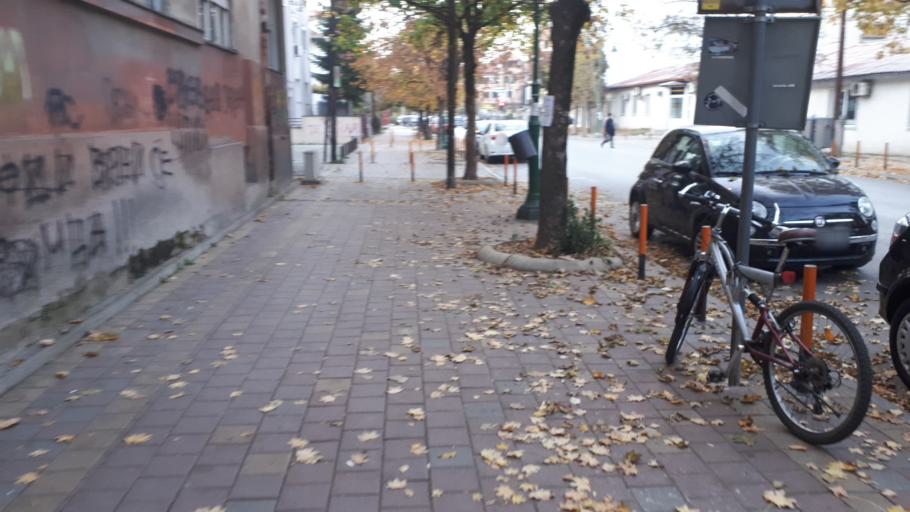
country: MK
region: Karpos
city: Skopje
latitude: 42.0035
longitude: 21.4167
